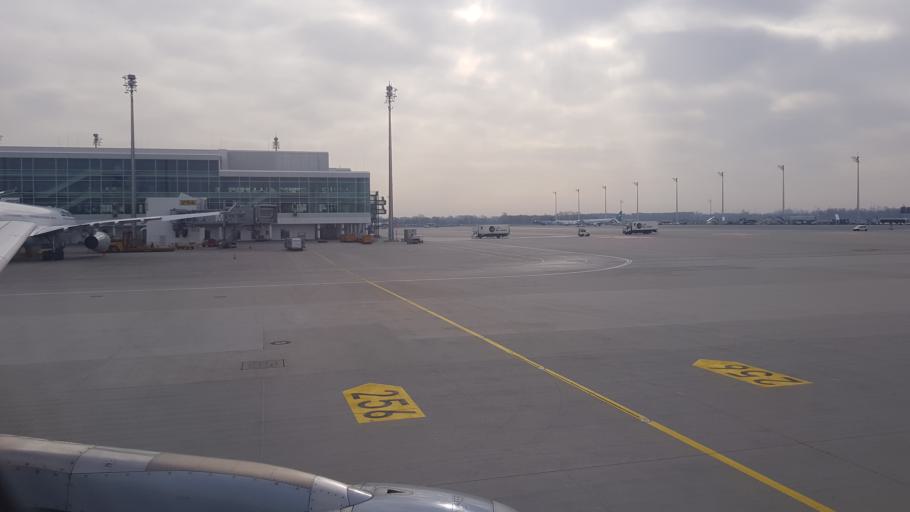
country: DE
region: Bavaria
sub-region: Upper Bavaria
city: Hallbergmoos
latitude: 48.3521
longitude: 11.7960
